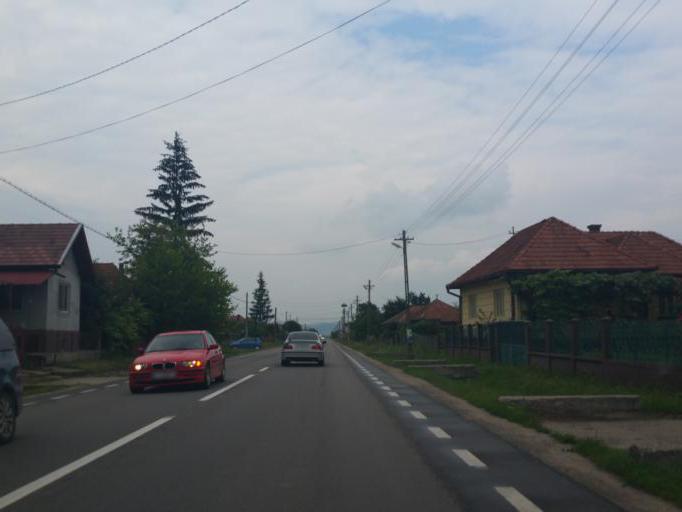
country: RO
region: Salaj
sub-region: Comuna Zimbor
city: Zimbor
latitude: 47.0045
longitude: 23.2579
